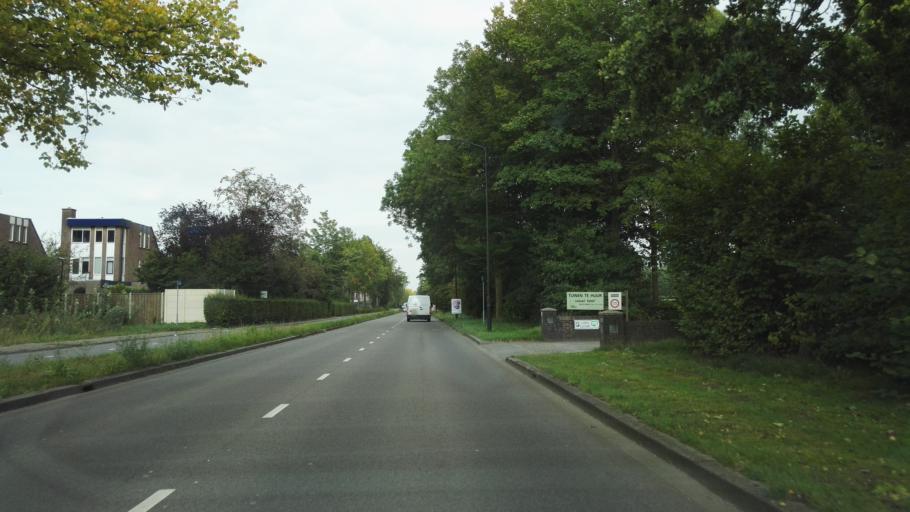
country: NL
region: Gelderland
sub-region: Gemeente Apeldoorn
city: Apeldoorn
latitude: 52.1830
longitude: 5.9967
